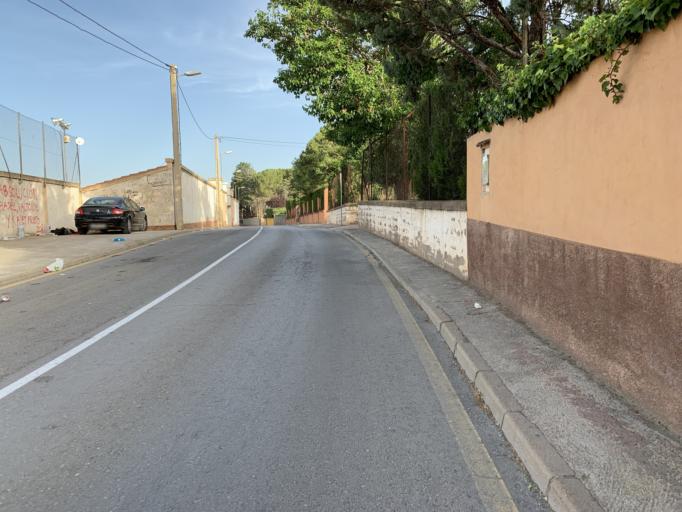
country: ES
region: Aragon
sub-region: Provincia de Teruel
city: Teruel
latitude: 40.3517
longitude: -1.1147
